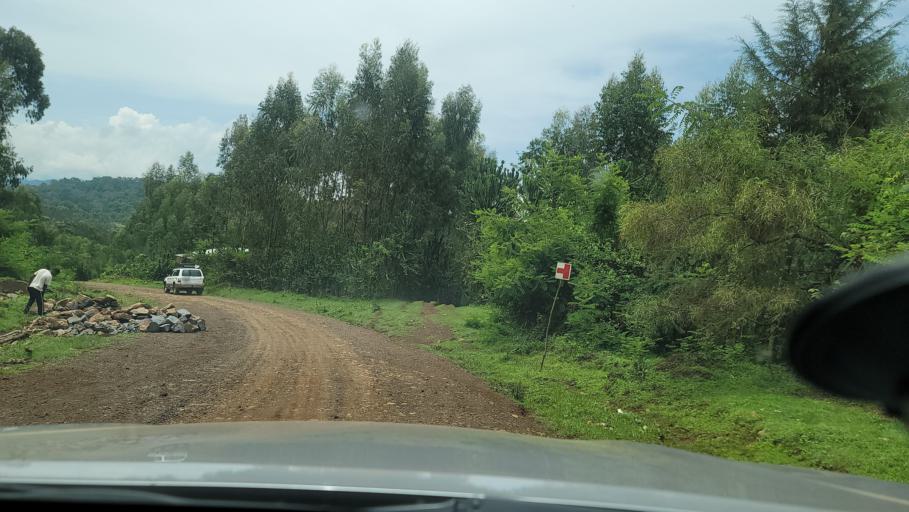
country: ET
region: Oromiya
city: Agaro
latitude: 7.7355
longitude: 36.2593
